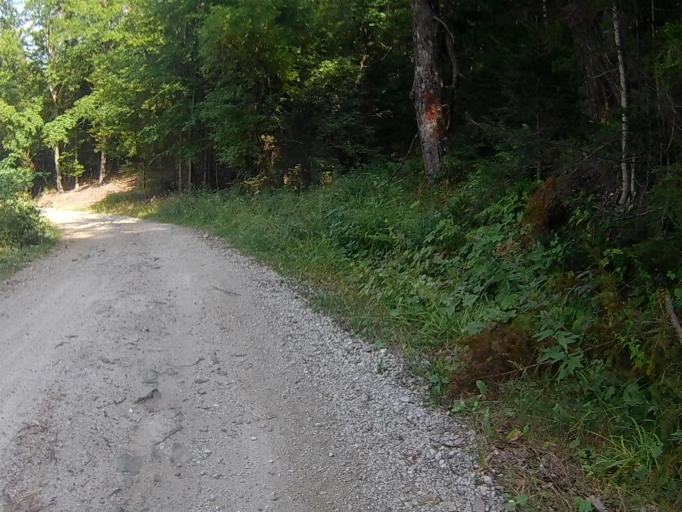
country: SI
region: Maribor
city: Pekre
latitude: 46.5225
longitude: 15.5782
